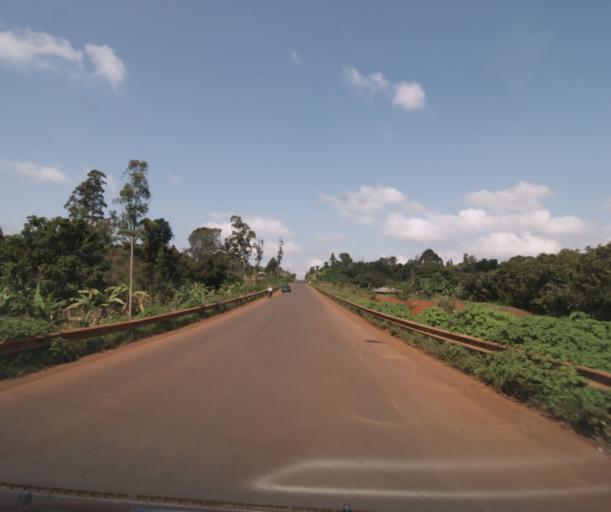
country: CM
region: West
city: Bansoa
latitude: 5.4993
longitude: 10.2336
